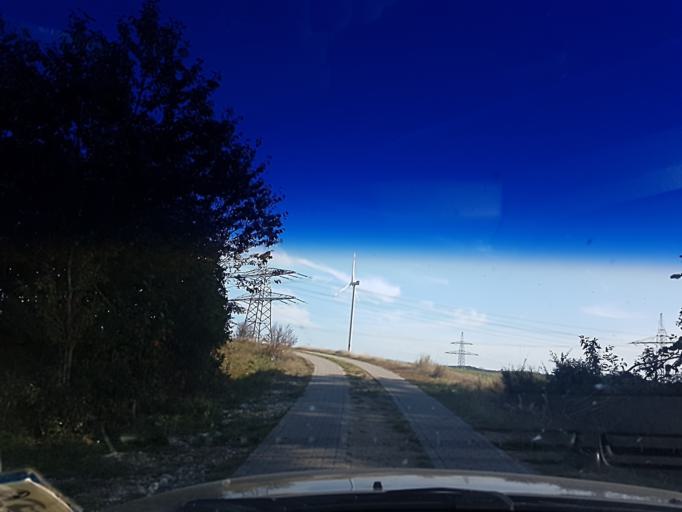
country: DE
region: Bavaria
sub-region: Upper Franconia
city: Poxdorf
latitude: 49.9851
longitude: 11.1071
